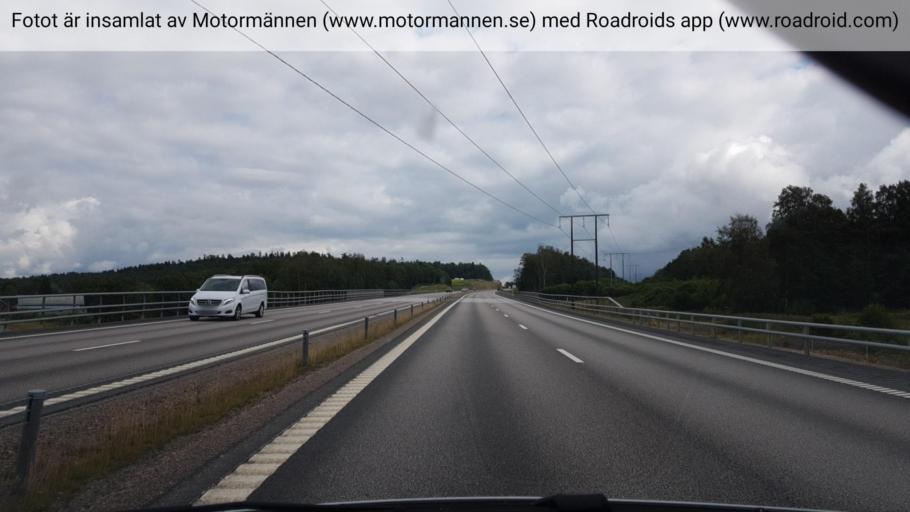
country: SE
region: Vaestra Goetaland
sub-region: Ulricehamns Kommun
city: Ulricehamn
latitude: 57.8098
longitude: 13.2367
